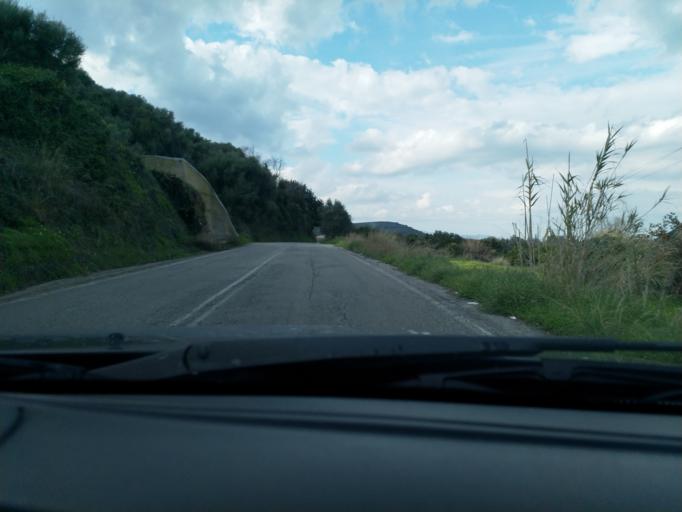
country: GR
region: Crete
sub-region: Nomos Chanias
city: Agia Marina
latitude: 35.4965
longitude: 23.9051
